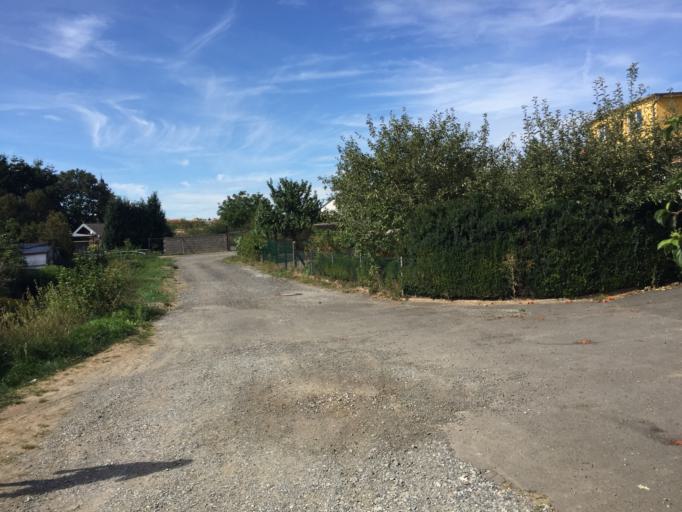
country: DE
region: Hesse
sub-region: Regierungsbezirk Giessen
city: Langgons
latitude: 50.4962
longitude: 8.6644
